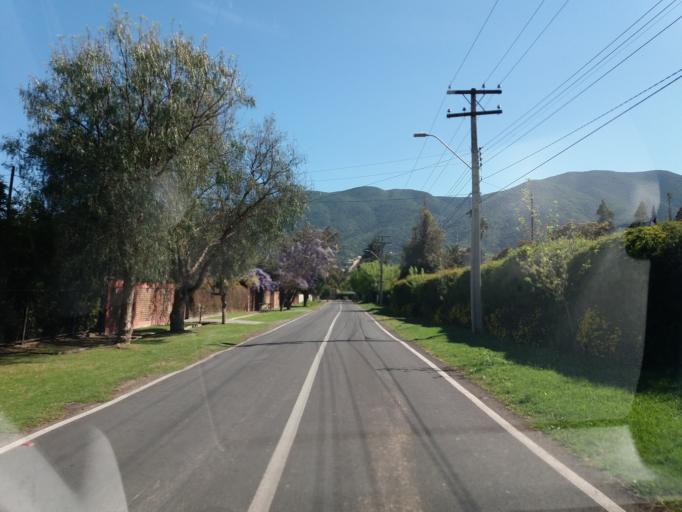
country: CL
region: Valparaiso
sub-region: Provincia de Marga Marga
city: Limache
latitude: -33.0011
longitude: -71.1924
